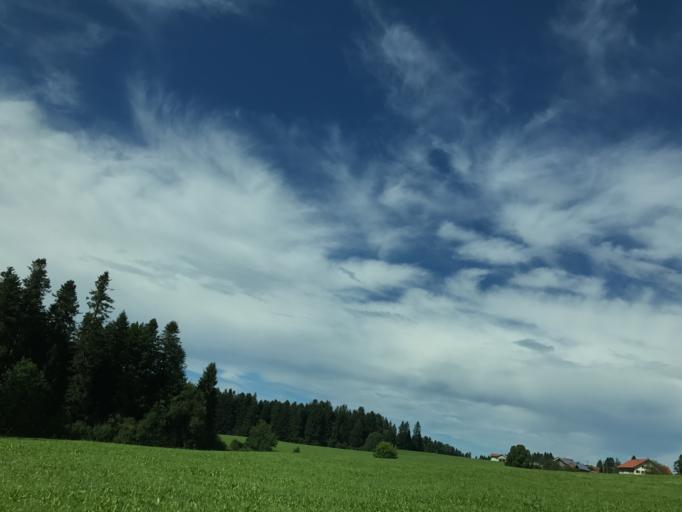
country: DE
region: Bavaria
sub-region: Swabia
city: Weiler-Simmerberg
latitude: 47.5982
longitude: 9.9406
